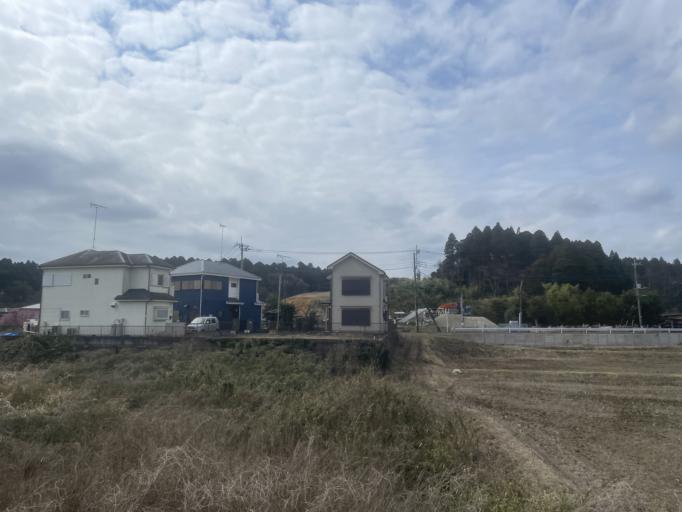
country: JP
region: Chiba
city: Yachimata
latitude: 35.6390
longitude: 140.3510
